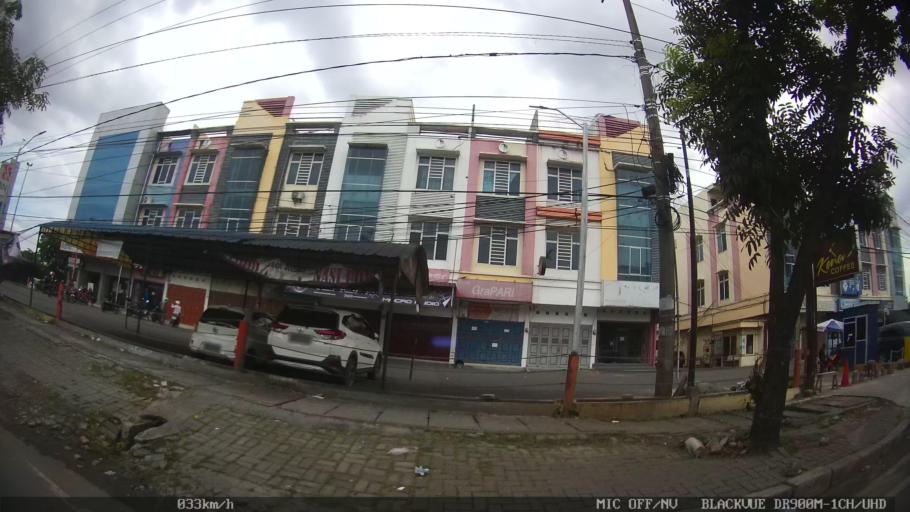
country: ID
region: North Sumatra
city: Sunggal
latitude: 3.5955
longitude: 98.6150
